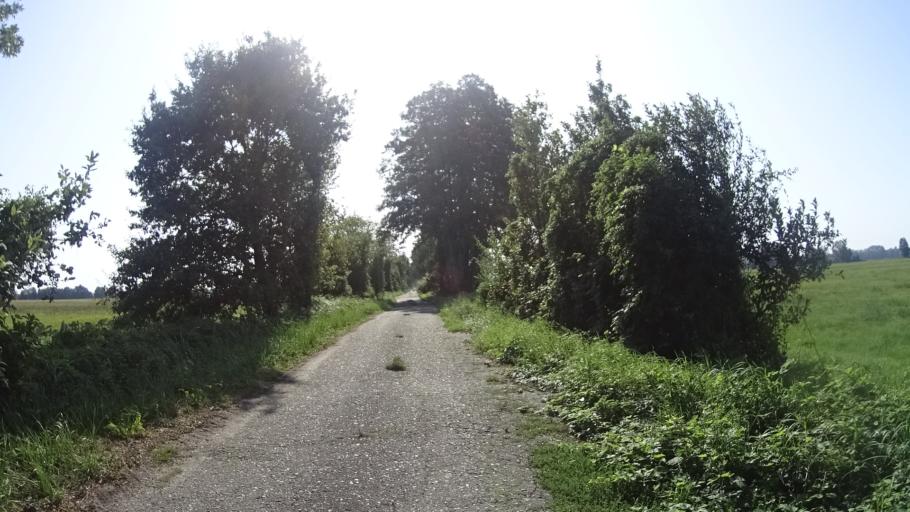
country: DE
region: Brandenburg
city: Neu Zauche
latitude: 51.9126
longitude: 14.0502
